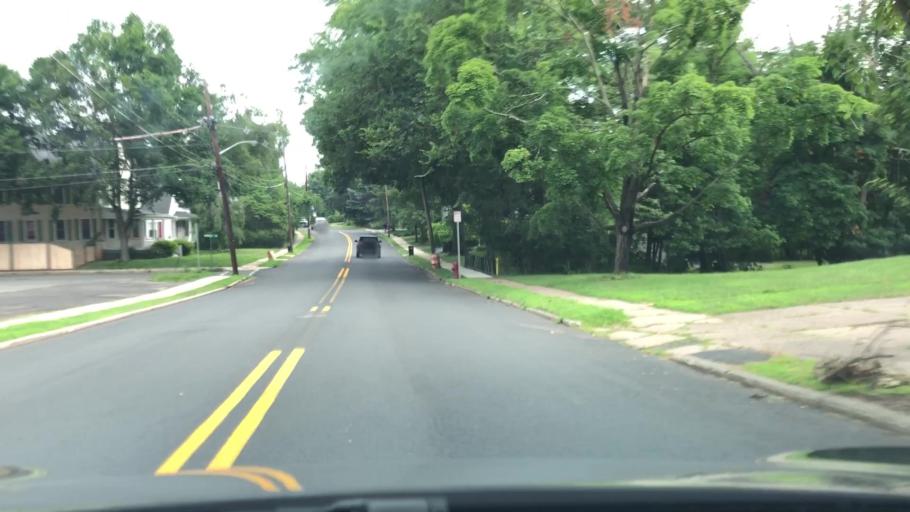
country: US
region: New Jersey
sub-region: Mercer County
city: Pennington
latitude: 40.3313
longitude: -74.7919
